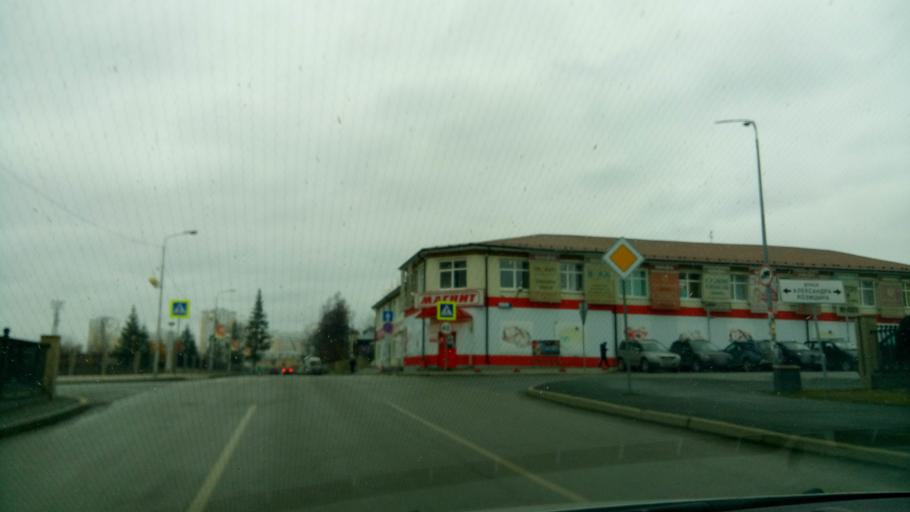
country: RU
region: Sverdlovsk
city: Verkhnyaya Pyshma
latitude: 56.9664
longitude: 60.5800
